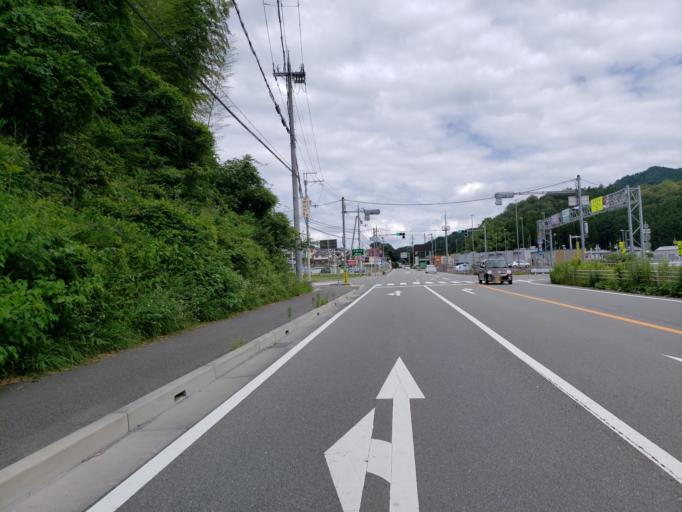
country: JP
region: Hyogo
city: Yamazakicho-nakabirose
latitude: 34.9642
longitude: 134.6916
